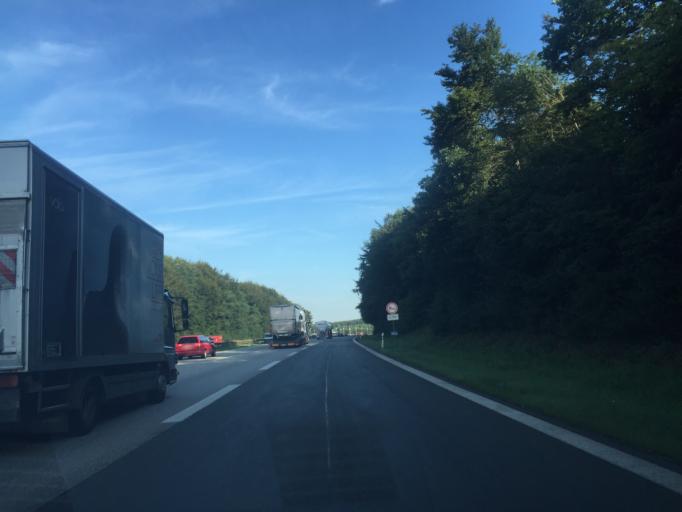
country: DE
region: Rheinland-Pfalz
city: Mudersbach
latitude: 50.8779
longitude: 7.9425
